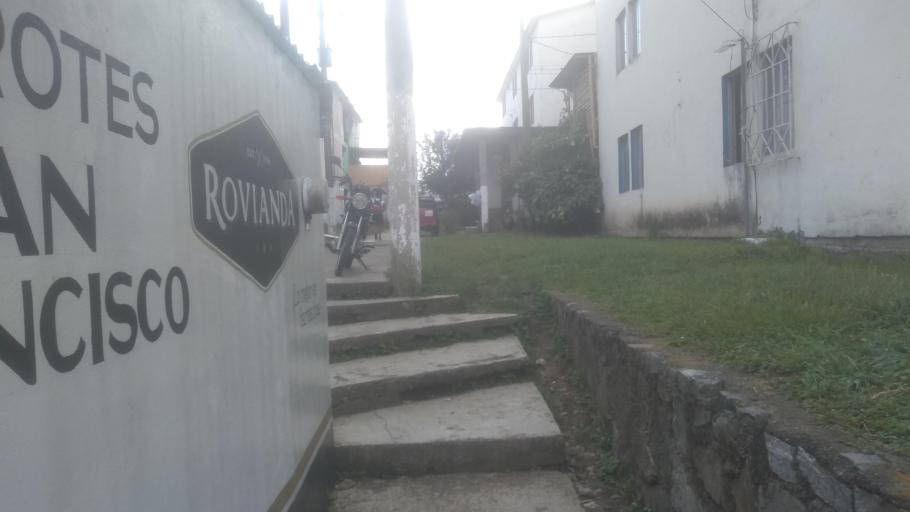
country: MX
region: Veracruz
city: Ixtac Zoquitlan
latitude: 18.8791
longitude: -97.0659
